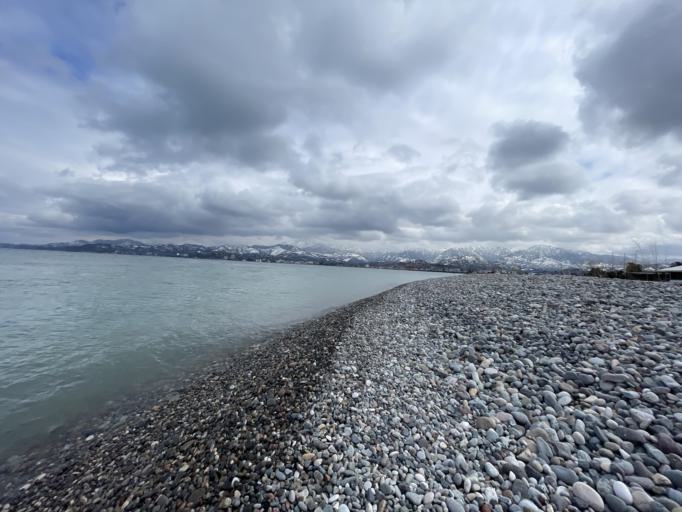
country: GE
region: Ajaria
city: Batumi
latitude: 41.6577
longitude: 41.6408
